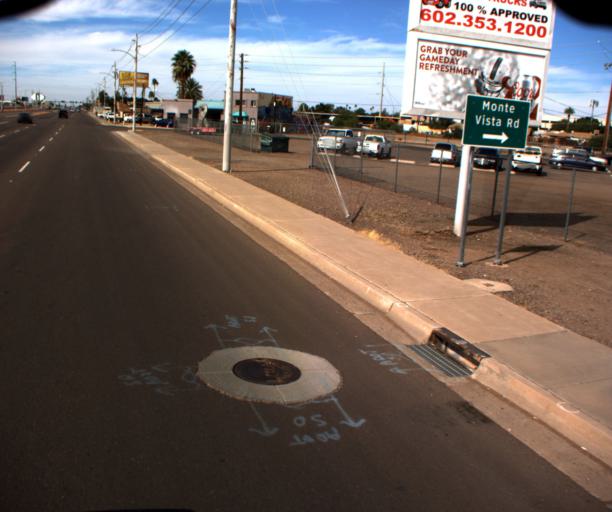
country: US
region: Arizona
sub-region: Maricopa County
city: Phoenix
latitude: 33.4703
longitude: -112.1050
